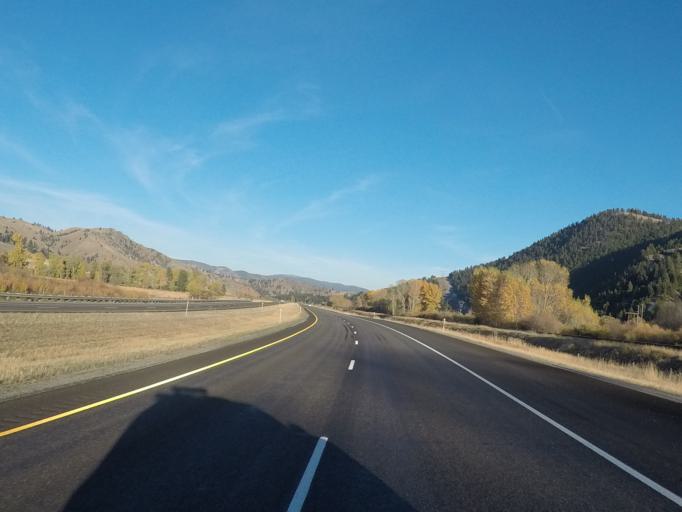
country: US
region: Montana
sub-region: Missoula County
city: Clinton
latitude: 46.6952
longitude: -113.4167
